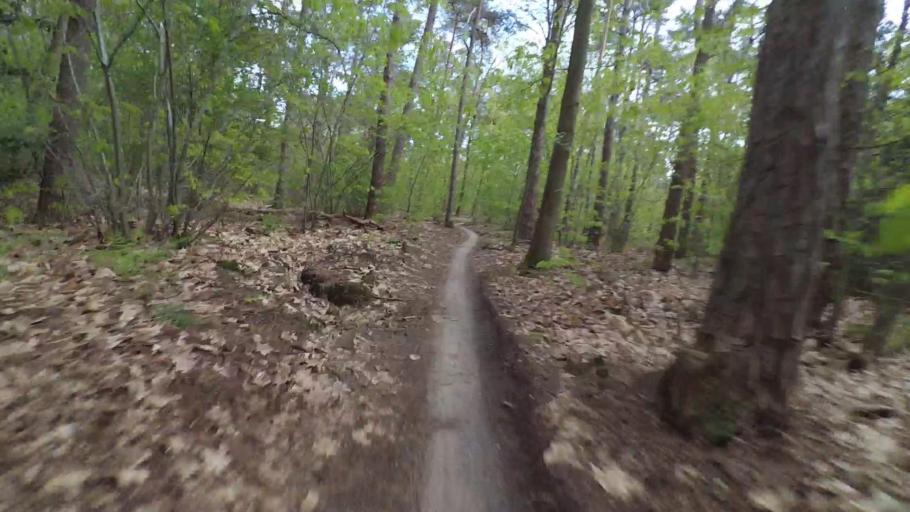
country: NL
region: Utrecht
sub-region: Gemeente Utrechtse Heuvelrug
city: Driebergen-Rijsenburg
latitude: 52.0767
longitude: 5.2749
